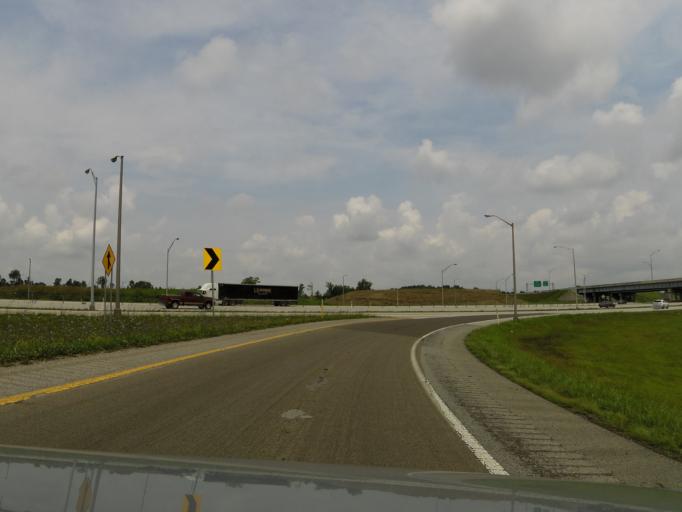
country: US
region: Kentucky
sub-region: Hardin County
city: Elizabethtown
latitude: 37.6715
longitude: -85.8511
